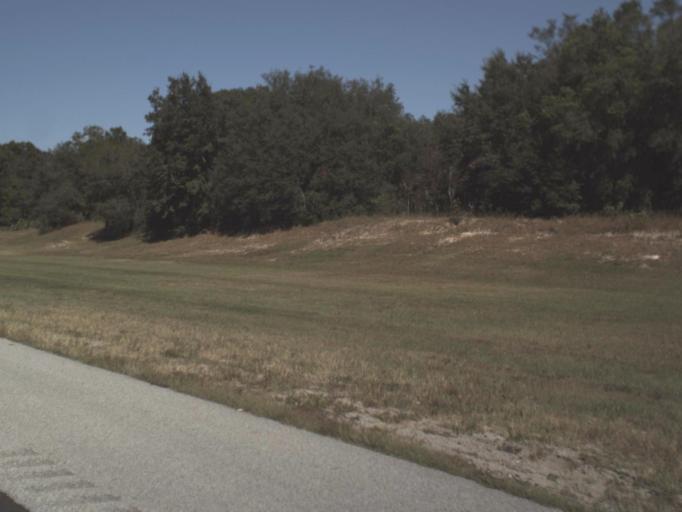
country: US
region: Florida
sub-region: Lake County
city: Hawthorne
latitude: 28.7196
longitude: -81.9009
